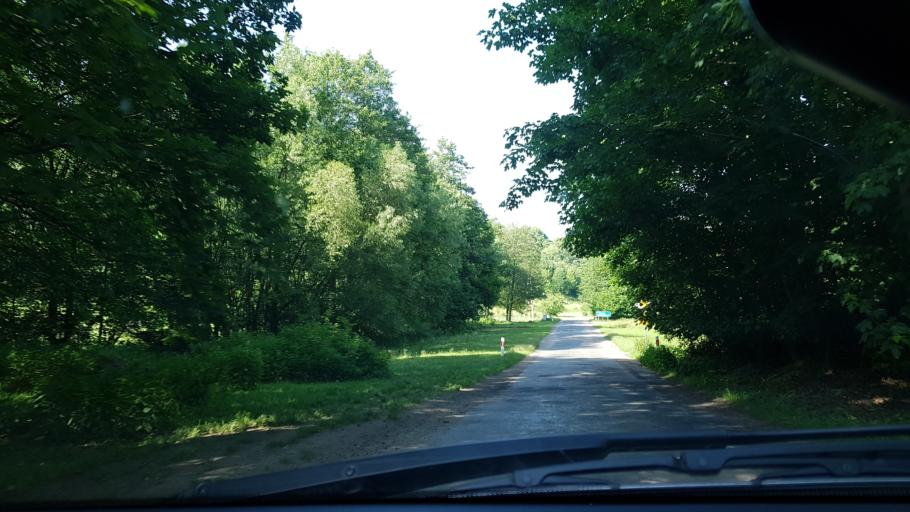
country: PL
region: Lower Silesian Voivodeship
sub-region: Powiat zabkowicki
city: Budzow
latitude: 50.5625
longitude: 16.6657
